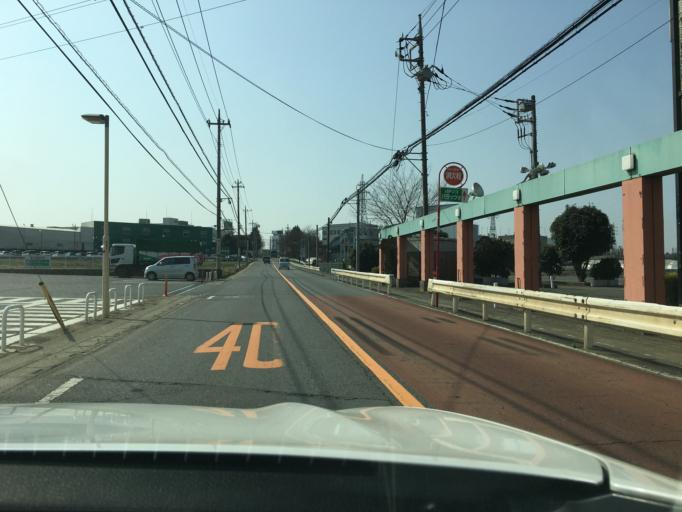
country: JP
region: Saitama
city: Kamifukuoka
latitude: 35.8560
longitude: 139.4691
